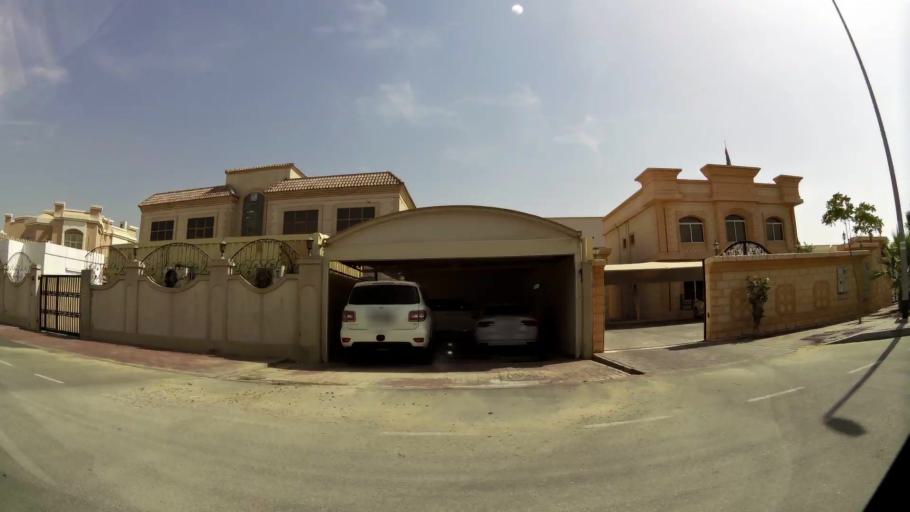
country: AE
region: Ash Shariqah
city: Sharjah
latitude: 25.2027
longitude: 55.4142
